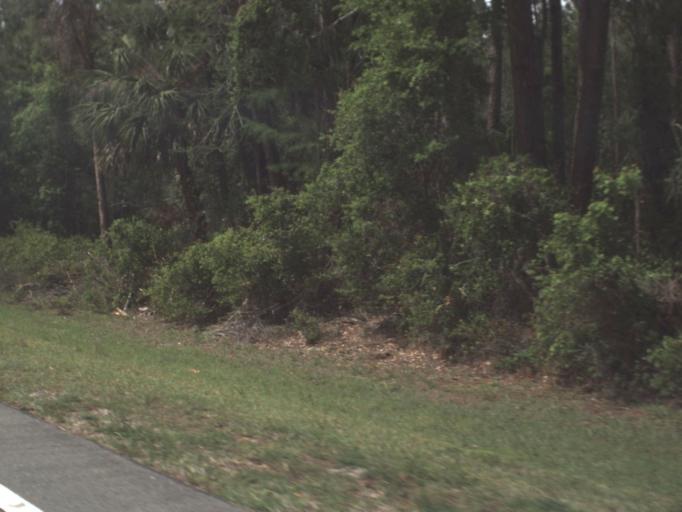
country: US
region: Florida
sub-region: Flagler County
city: Bunnell
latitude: 29.4744
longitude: -81.3288
